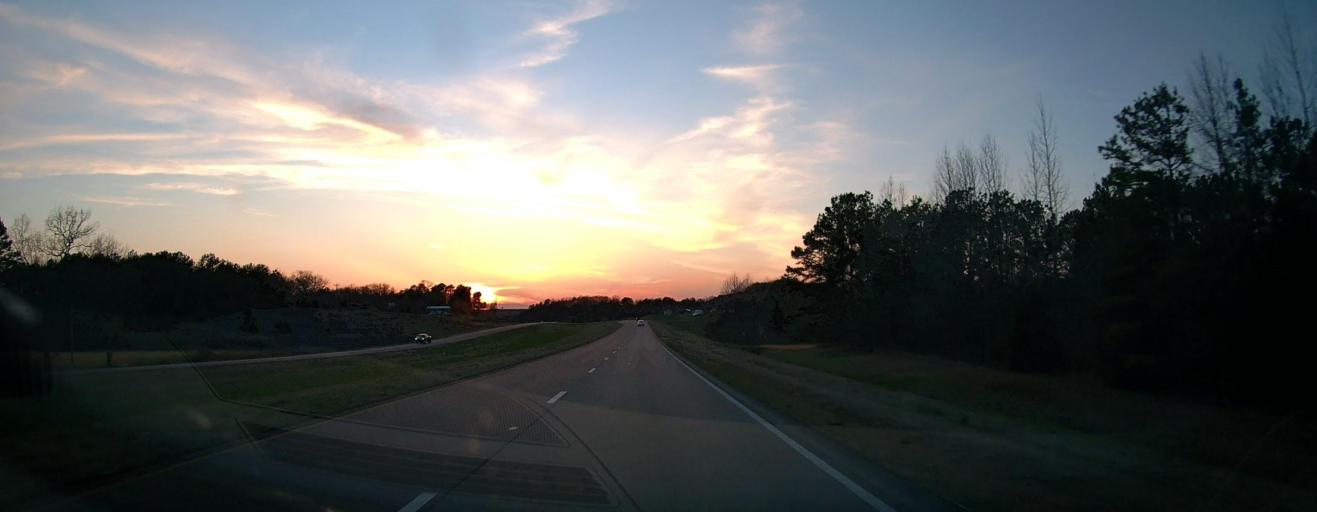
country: US
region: Mississippi
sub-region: Tippah County
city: Ripley
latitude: 34.9551
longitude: -88.8458
